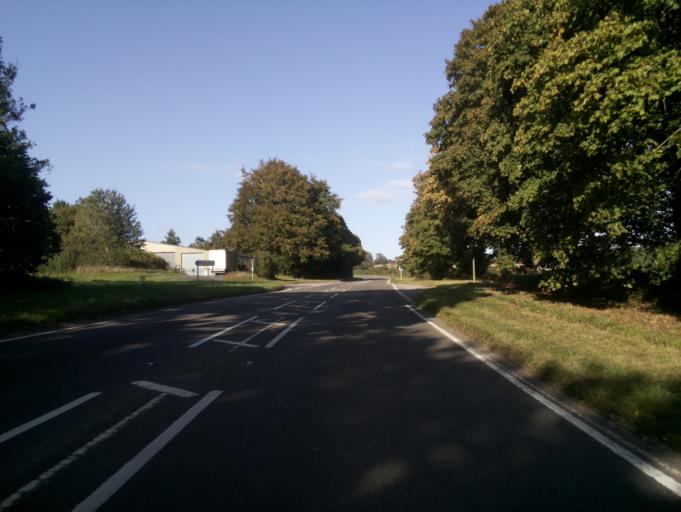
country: GB
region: England
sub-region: Hampshire
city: Four Marks
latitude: 51.0343
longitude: -1.0735
